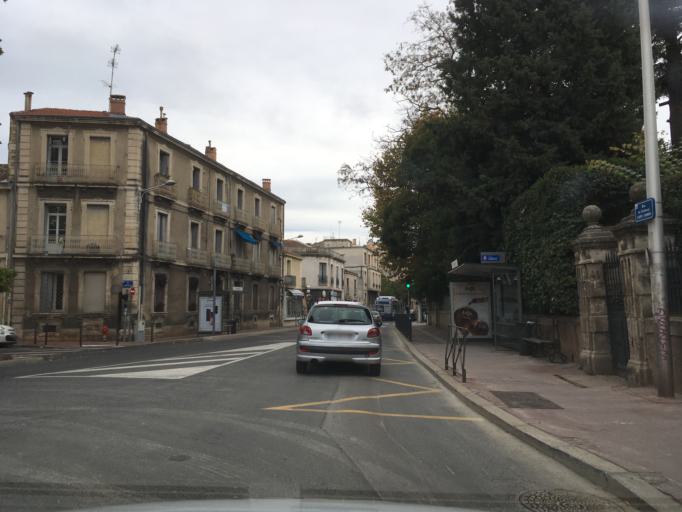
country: FR
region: Languedoc-Roussillon
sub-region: Departement de l'Herault
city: Montpellier
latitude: 43.6155
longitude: 3.8694
